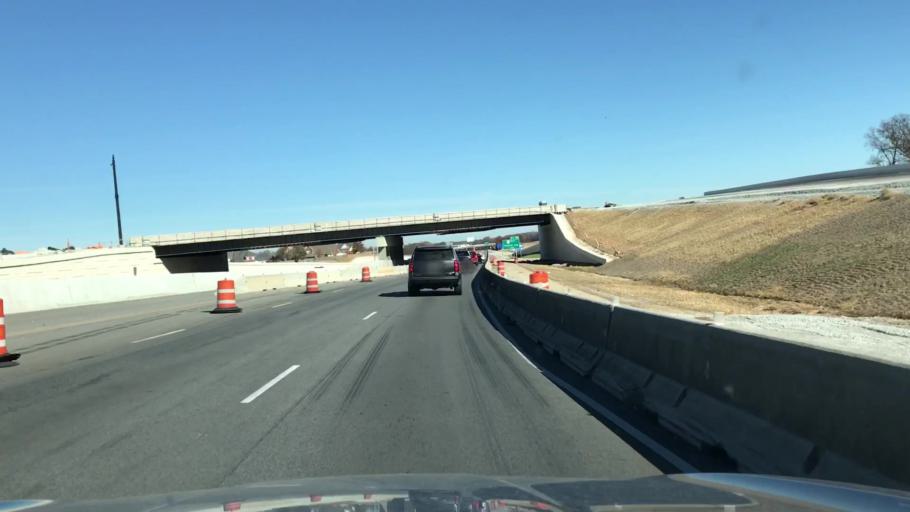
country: US
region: Arkansas
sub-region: Benton County
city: Bentonville
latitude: 36.3627
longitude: -94.1764
